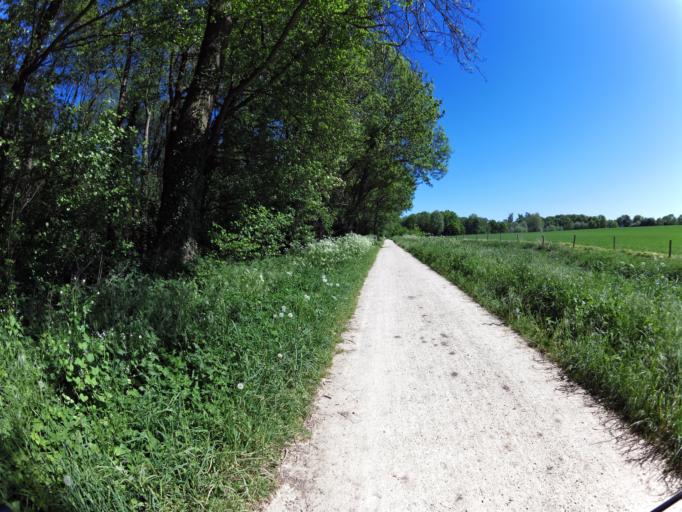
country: NL
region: Limburg
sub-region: Gemeente Onderbanken
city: Merkelbeek
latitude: 50.9885
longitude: 5.9487
